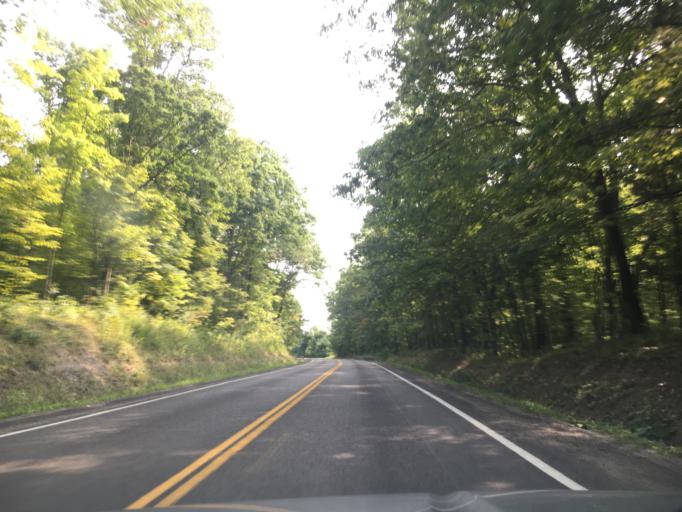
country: US
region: New York
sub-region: Steuben County
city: Sylvan Beach
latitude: 42.4806
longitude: -77.1255
